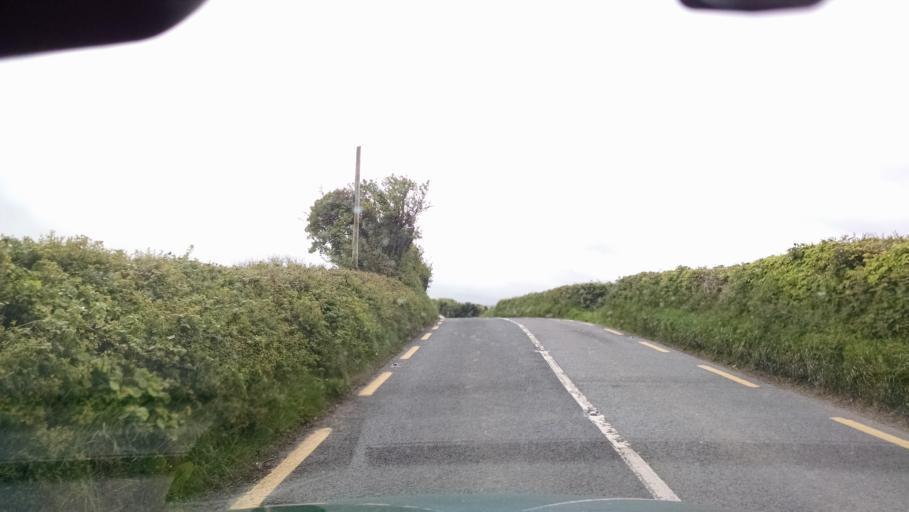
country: IE
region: Connaught
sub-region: County Galway
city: Bearna
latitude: 53.1095
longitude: -9.1538
